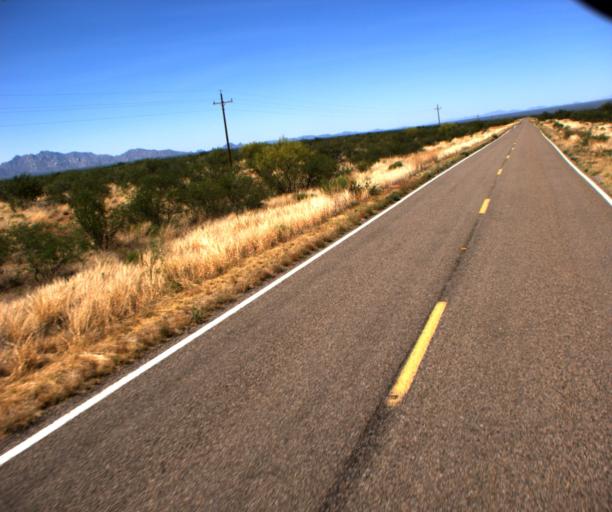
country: US
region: Arizona
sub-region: Pima County
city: Three Points
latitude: 31.7669
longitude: -111.4705
